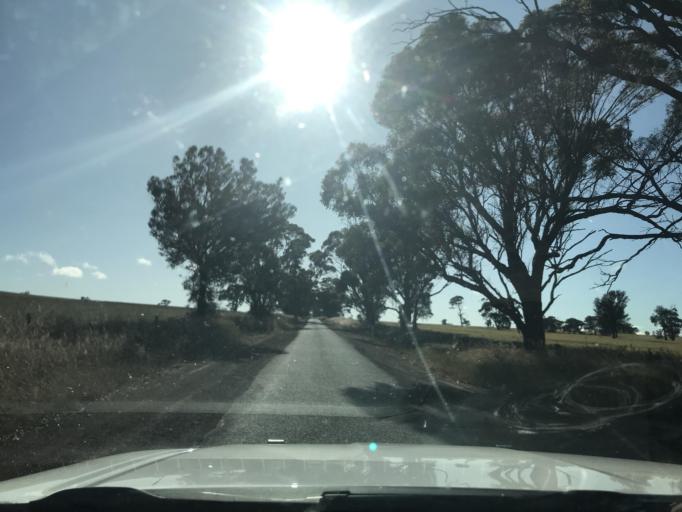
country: AU
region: Victoria
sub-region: Horsham
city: Horsham
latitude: -36.6973
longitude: 141.5975
